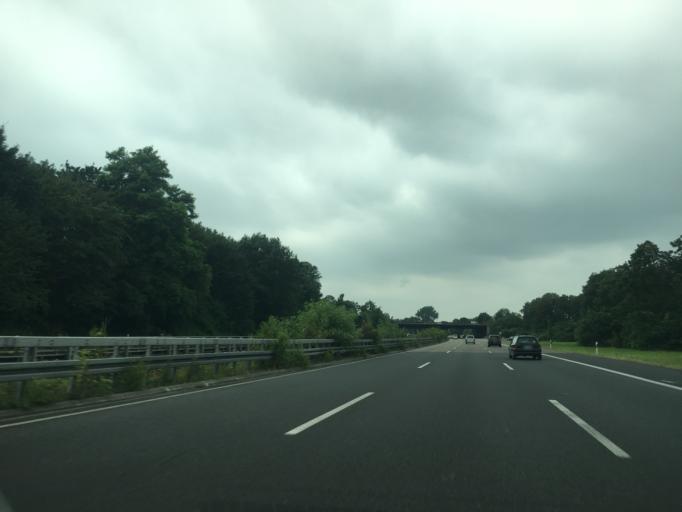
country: DE
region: North Rhine-Westphalia
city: Meiderich
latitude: 51.4868
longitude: 6.8193
